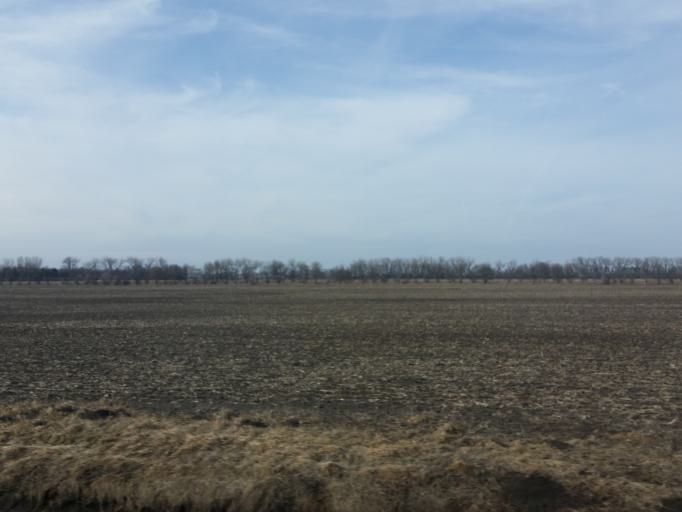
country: US
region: Minnesota
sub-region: Wilkin County
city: Breckenridge
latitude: 46.4712
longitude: -96.5567
